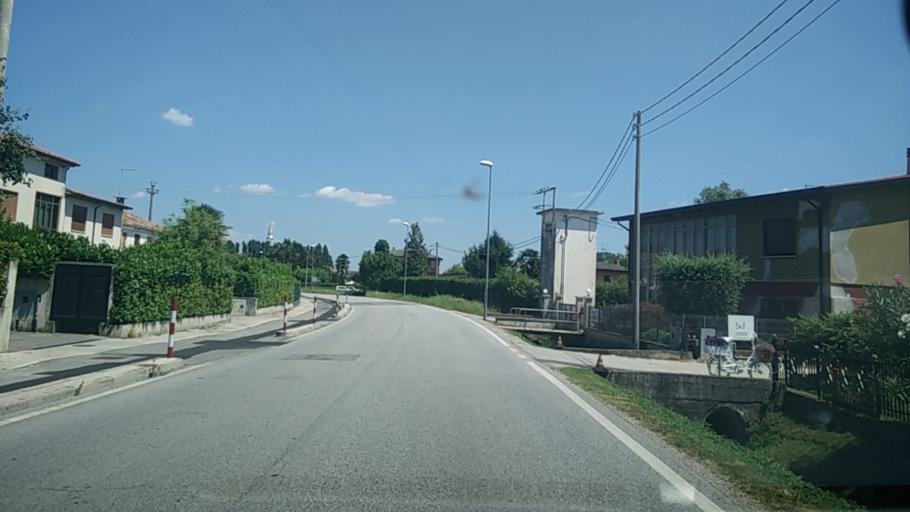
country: IT
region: Veneto
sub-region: Provincia di Padova
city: Cittadella
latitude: 45.6192
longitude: 11.7971
